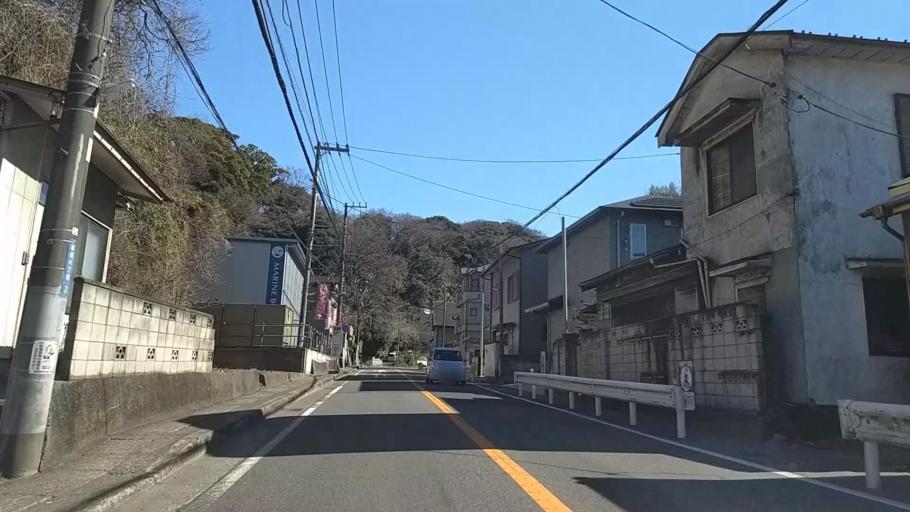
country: JP
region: Kanagawa
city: Kamakura
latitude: 35.3196
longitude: 139.5291
